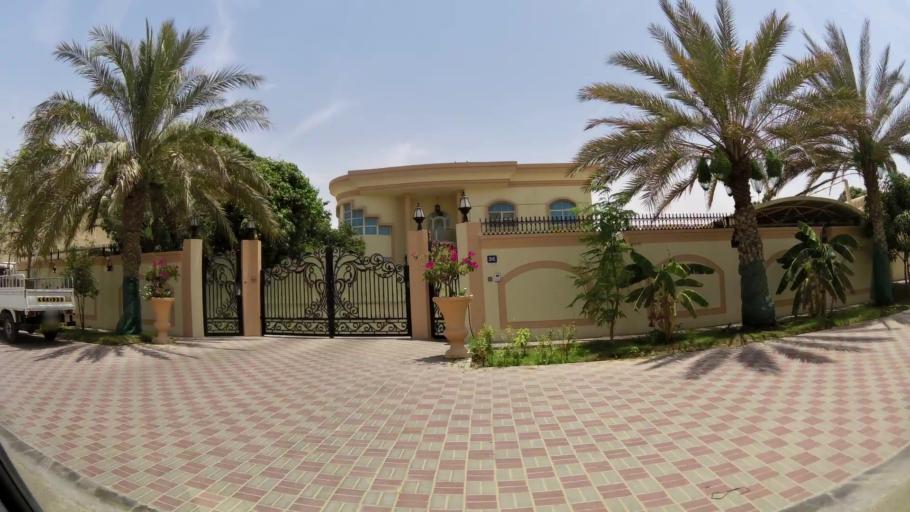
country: AE
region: Ash Shariqah
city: Sharjah
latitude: 25.2505
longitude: 55.4664
